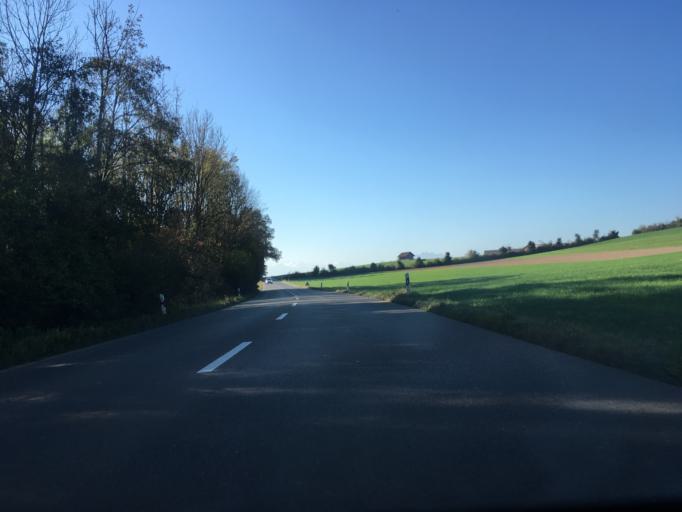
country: CH
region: Zug
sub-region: Zug
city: Baar
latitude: 47.2203
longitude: 8.5212
